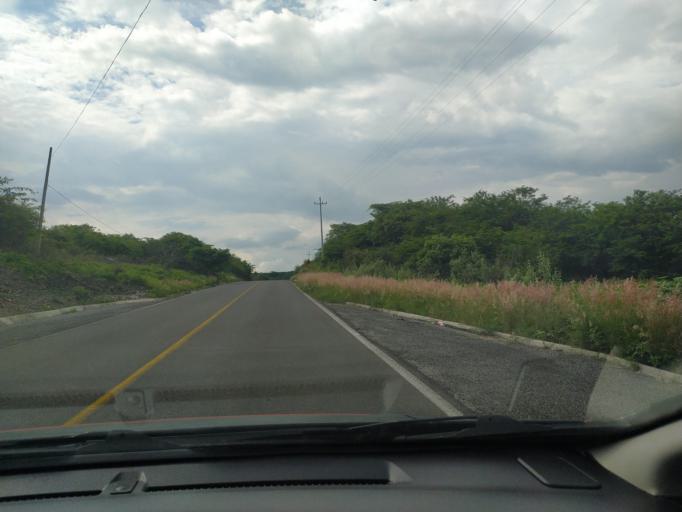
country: MX
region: Jalisco
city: Villa Corona
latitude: 20.3768
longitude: -103.6715
